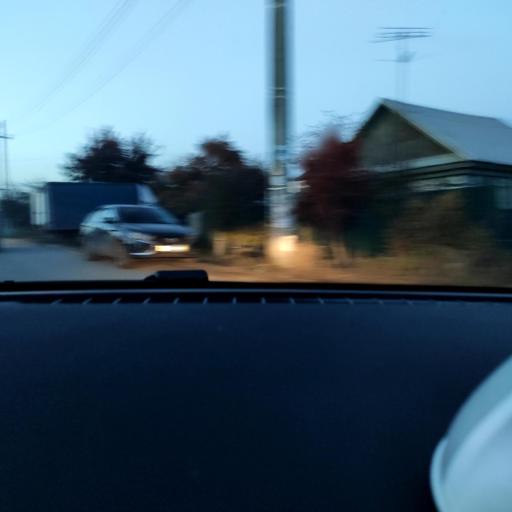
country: RU
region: Samara
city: Petra-Dubrava
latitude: 53.2941
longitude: 50.3094
